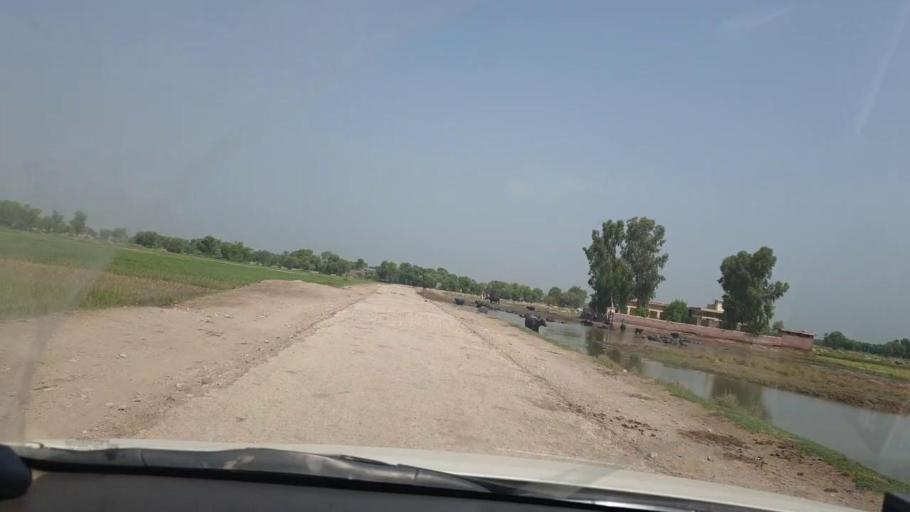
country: PK
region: Sindh
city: Chak
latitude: 27.8774
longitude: 68.7831
